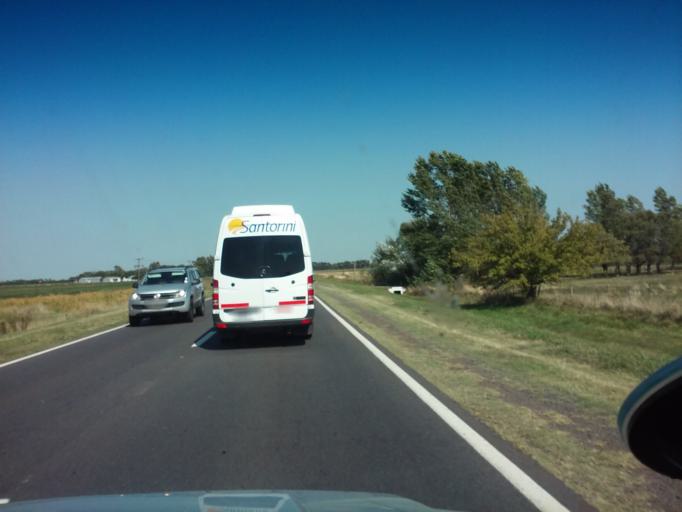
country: AR
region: Buenos Aires
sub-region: Partido de Chivilcoy
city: Chivilcoy
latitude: -34.9565
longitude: -60.0280
